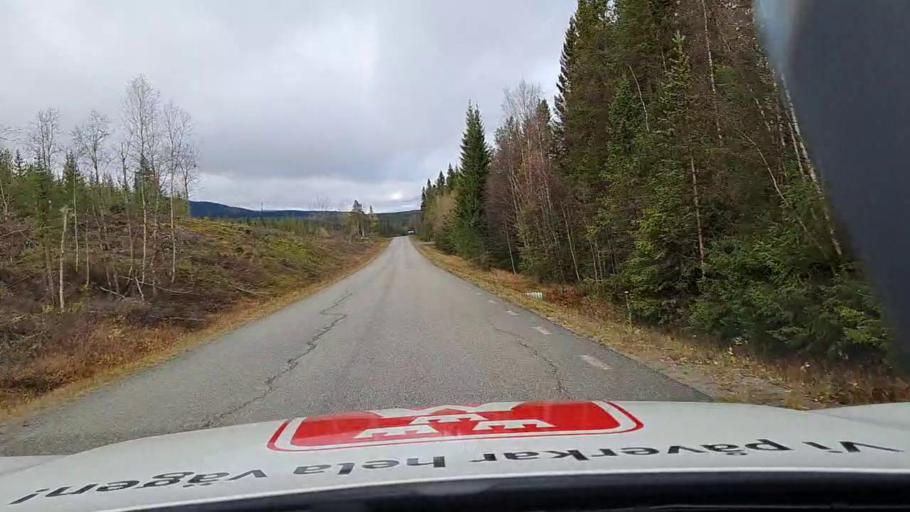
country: SE
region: Jaemtland
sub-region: Bergs Kommun
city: Hoverberg
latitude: 63.0399
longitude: 14.0159
